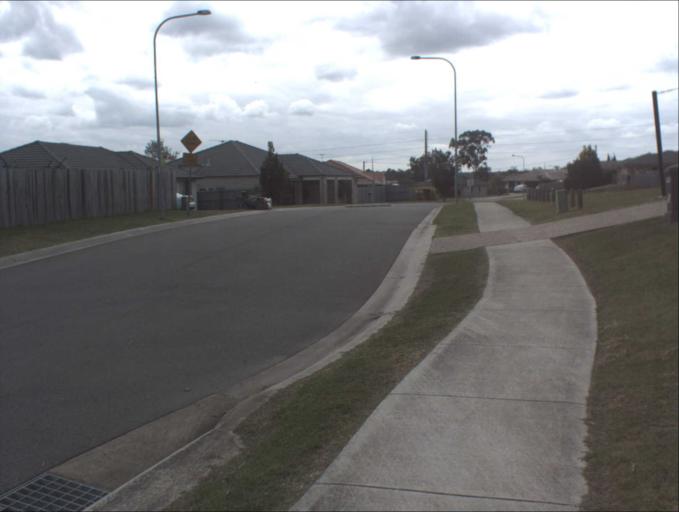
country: AU
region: Queensland
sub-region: Logan
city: Logan City
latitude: -27.6718
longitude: 153.0836
